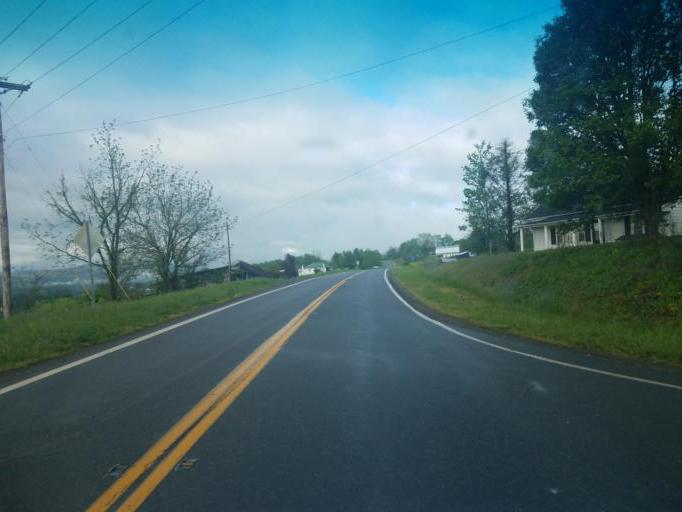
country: US
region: Virginia
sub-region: Washington County
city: Emory
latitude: 36.7057
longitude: -81.7841
